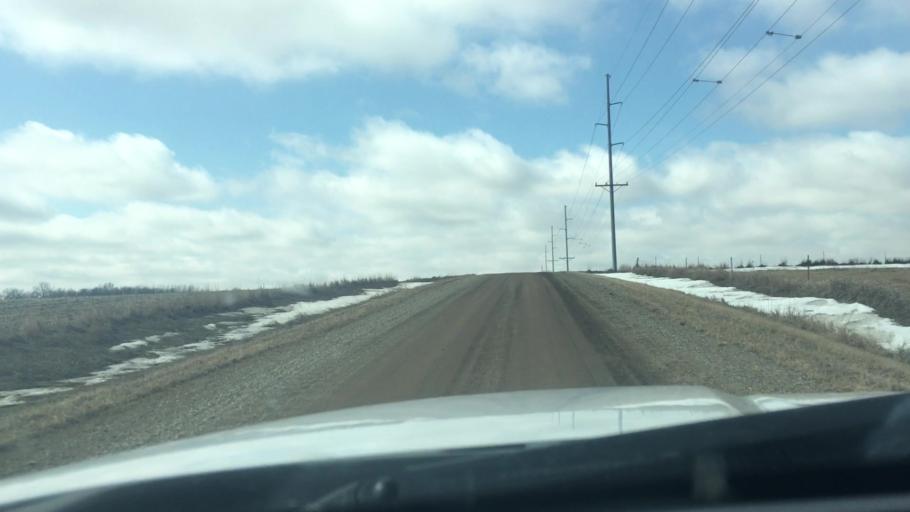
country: US
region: South Dakota
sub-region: Minnehaha County
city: Crooks
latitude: 43.6164
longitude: -96.8025
